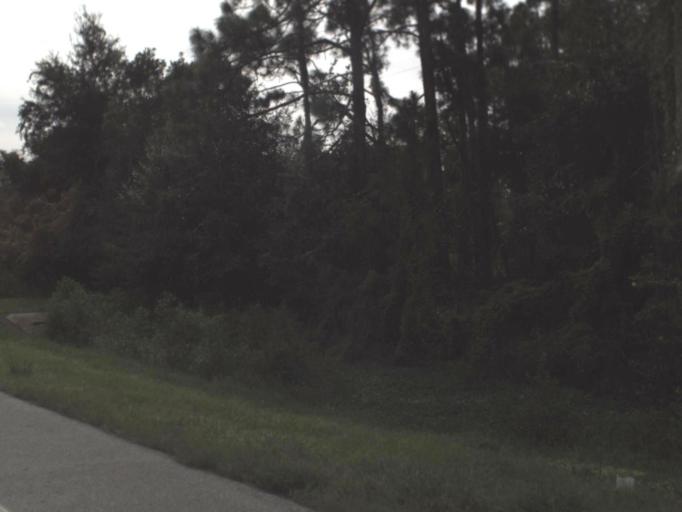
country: US
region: Florida
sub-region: Highlands County
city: Placid Lakes
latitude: 27.2097
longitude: -81.3436
